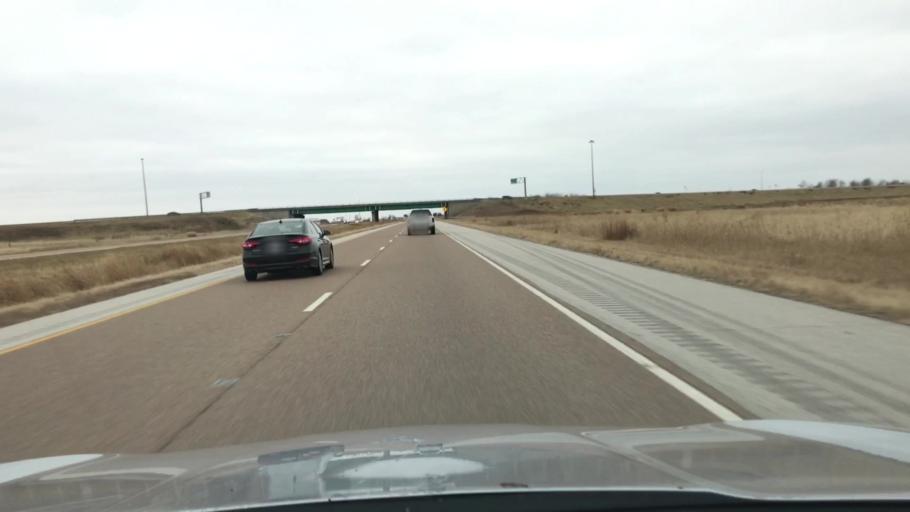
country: US
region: Illinois
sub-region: Montgomery County
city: Litchfield
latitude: 39.1786
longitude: -89.6797
